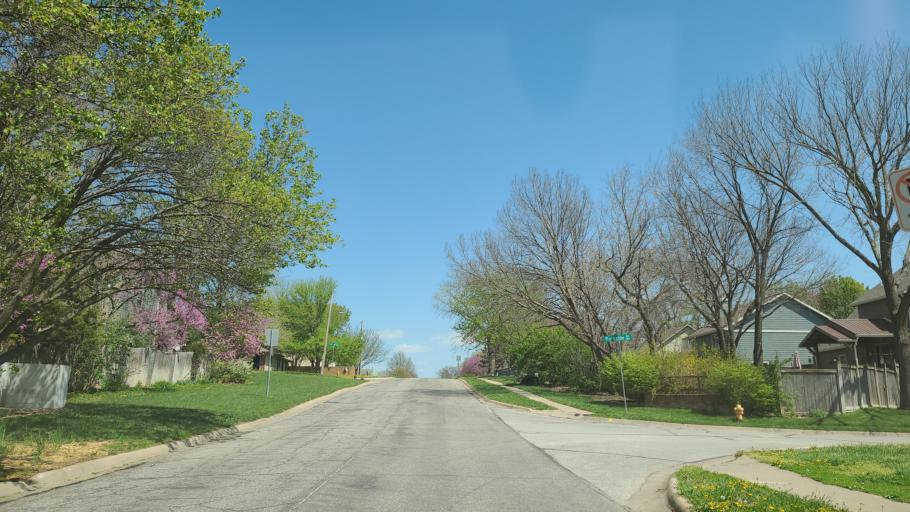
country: US
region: Kansas
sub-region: Douglas County
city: Lawrence
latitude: 38.9643
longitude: -95.2840
